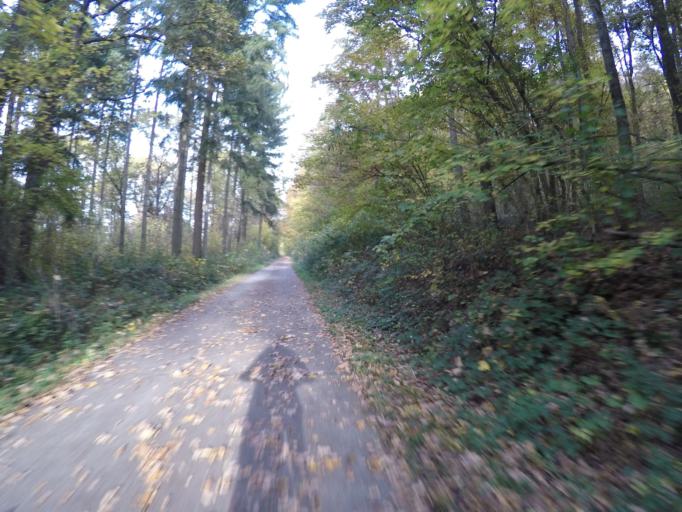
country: BE
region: Wallonia
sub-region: Province du Luxembourg
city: Hotton
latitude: 50.2735
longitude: 5.4743
